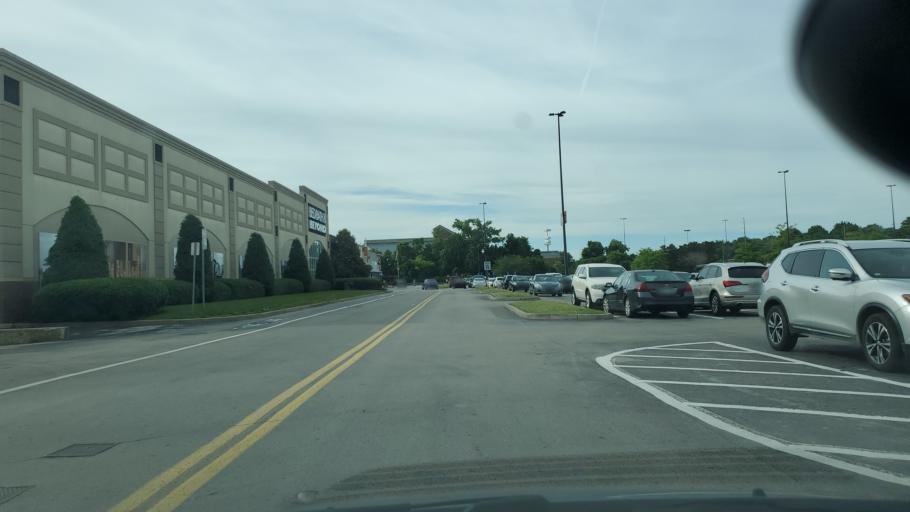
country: US
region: Tennessee
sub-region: Davidson County
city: Lakewood
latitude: 36.2029
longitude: -86.6909
